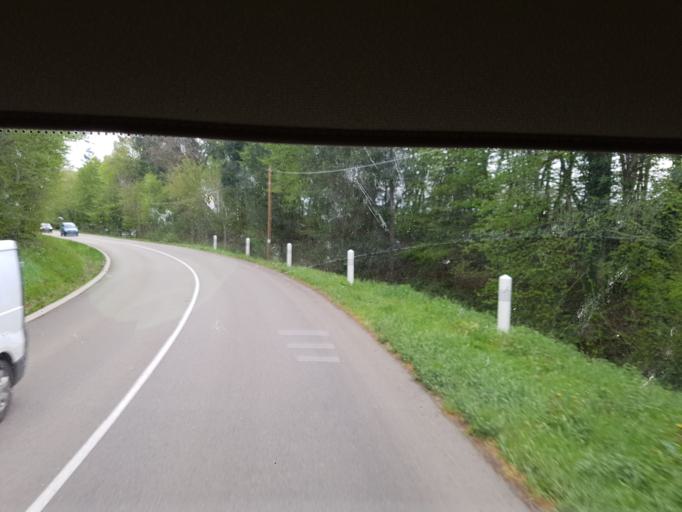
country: FR
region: Bourgogne
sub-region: Departement de Saone-et-Loire
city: Charolles
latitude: 46.4505
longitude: 4.2743
